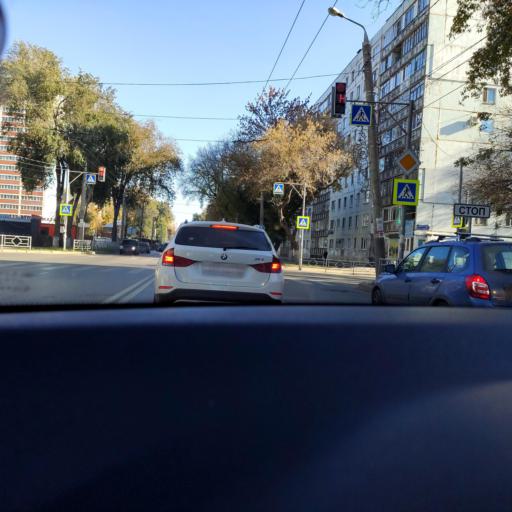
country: RU
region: Samara
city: Samara
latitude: 53.2279
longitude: 50.2648
